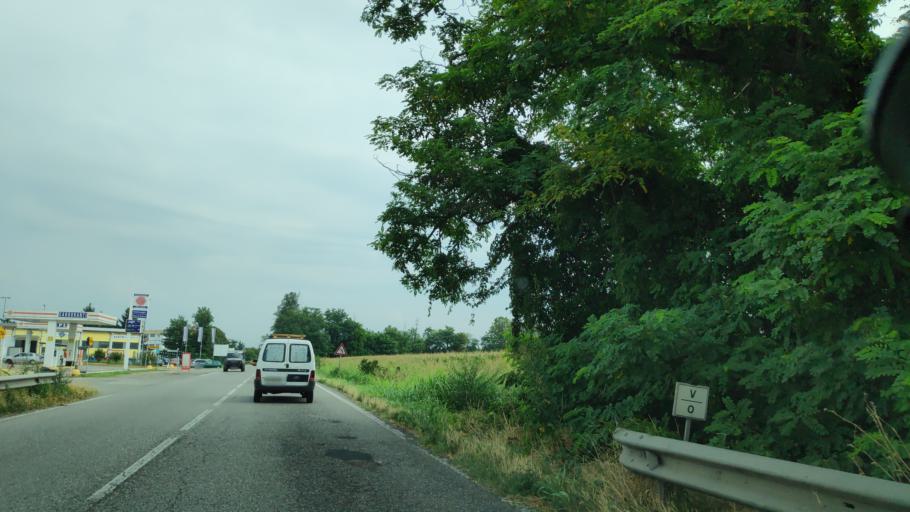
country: IT
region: Lombardy
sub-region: Citta metropolitana di Milano
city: Melegnano
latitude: 45.3620
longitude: 9.3362
